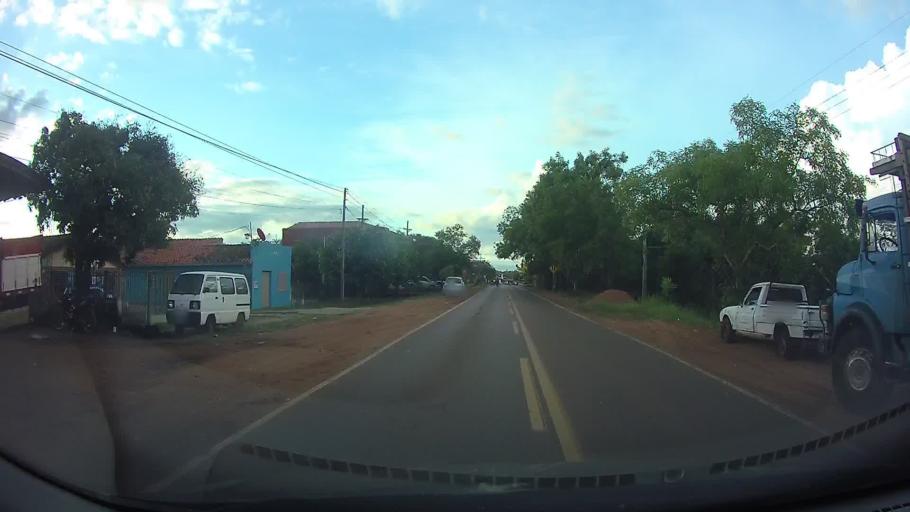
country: PY
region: Paraguari
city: Carapegua
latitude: -25.7692
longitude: -57.2349
